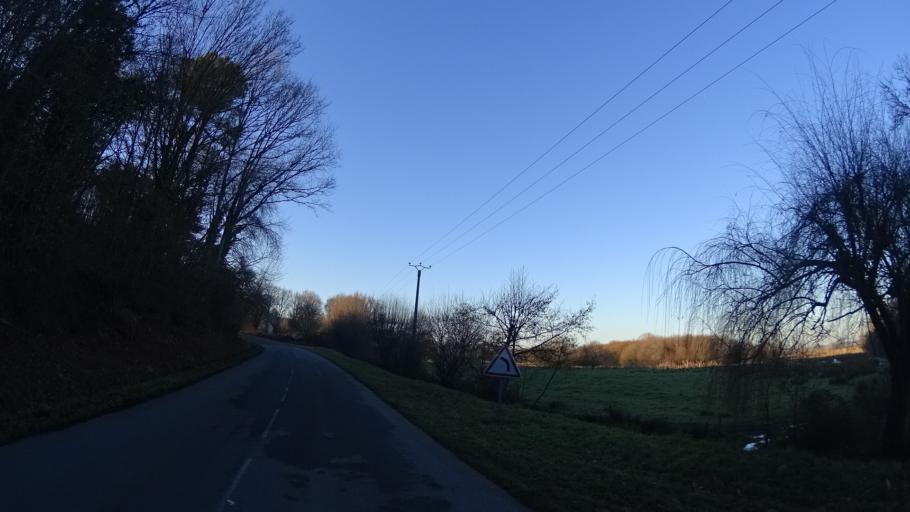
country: FR
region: Brittany
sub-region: Departement du Morbihan
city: Saint-Jean-la-Poterie
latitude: 47.6438
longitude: -2.1162
